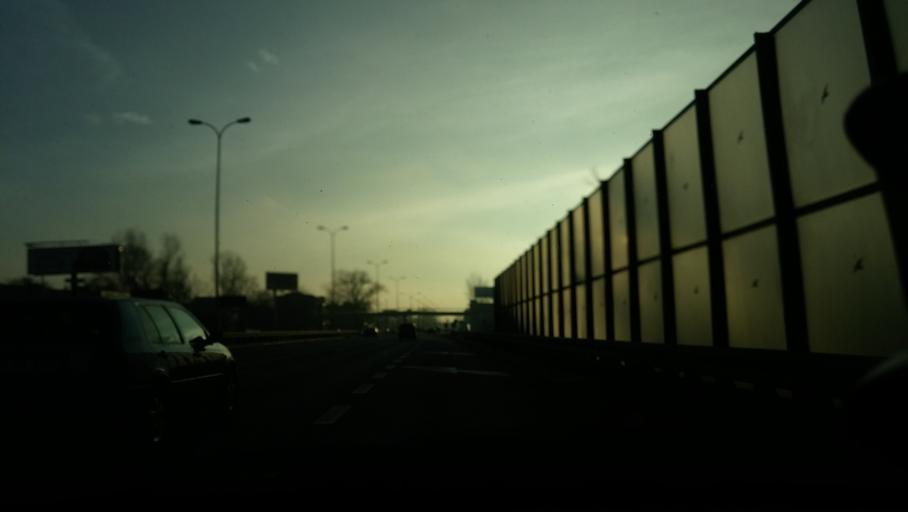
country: PL
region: Masovian Voivodeship
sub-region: Warszawa
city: Rembertow
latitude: 52.2310
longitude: 21.1341
